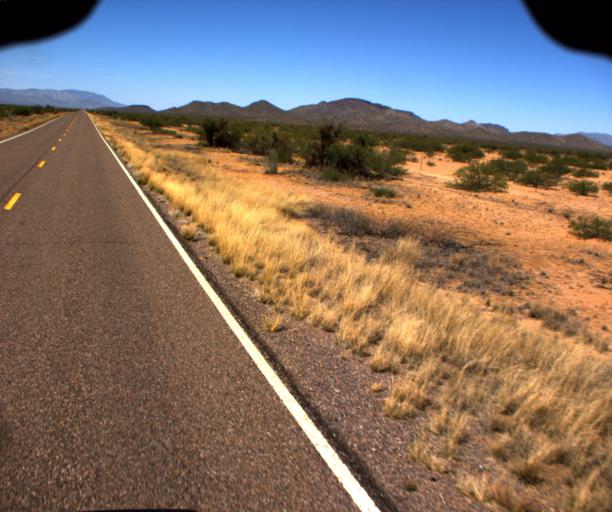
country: US
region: Arizona
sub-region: Yavapai County
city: Congress
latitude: 34.0571
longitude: -113.0501
